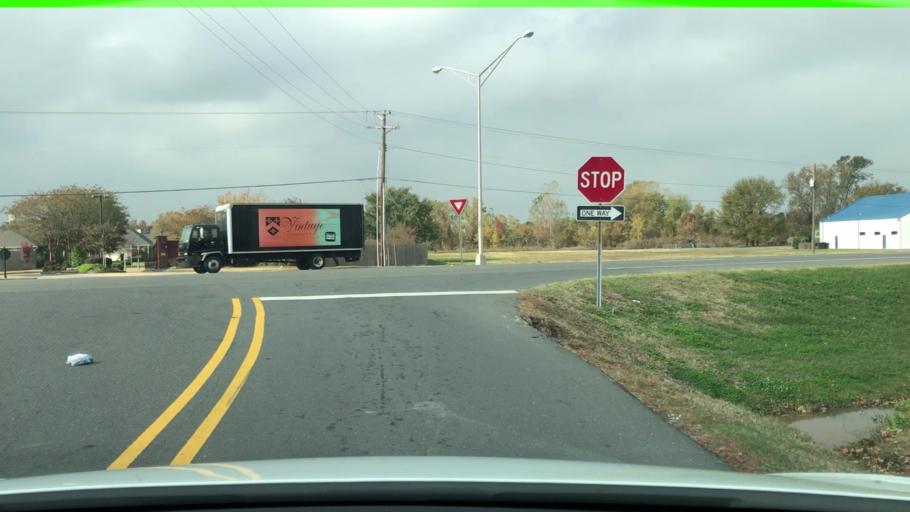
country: US
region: Louisiana
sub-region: Bossier Parish
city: Bossier City
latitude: 32.4082
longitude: -93.6978
